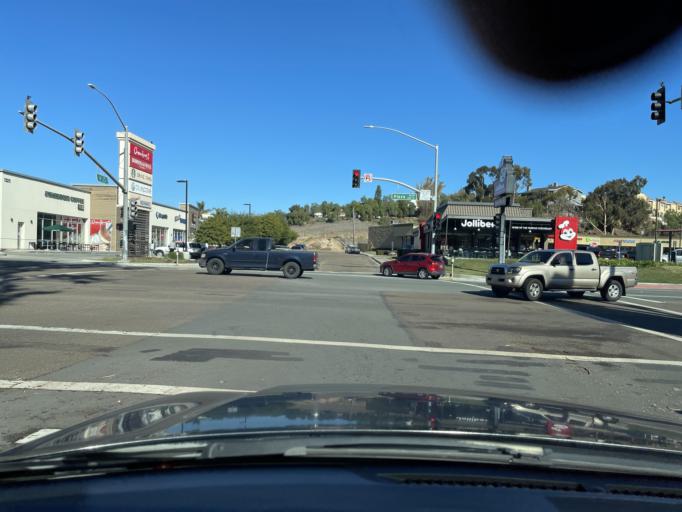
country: US
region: California
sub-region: San Diego County
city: National City
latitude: 32.6767
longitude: -117.0920
